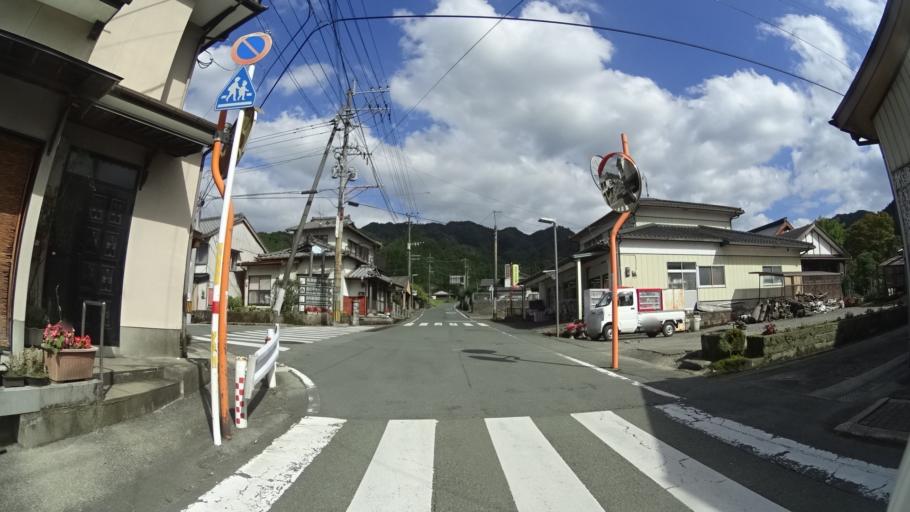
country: JP
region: Kumamoto
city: Aso
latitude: 32.8169
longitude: 131.1278
